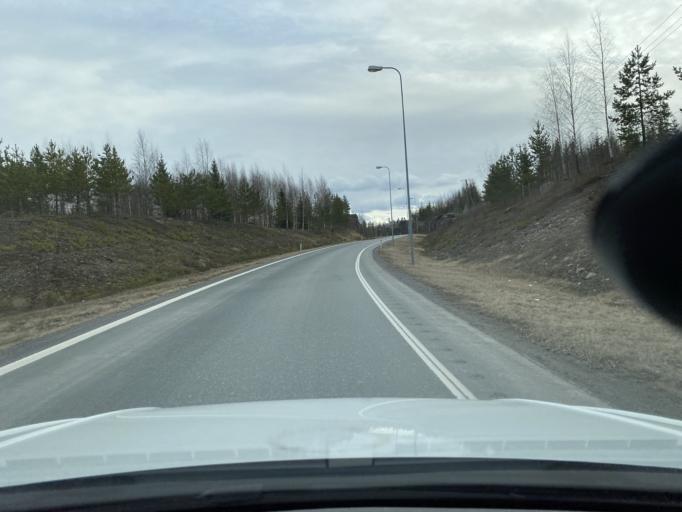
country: FI
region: Pirkanmaa
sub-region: Tampere
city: Lempaeaelae
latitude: 61.3681
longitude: 23.7890
